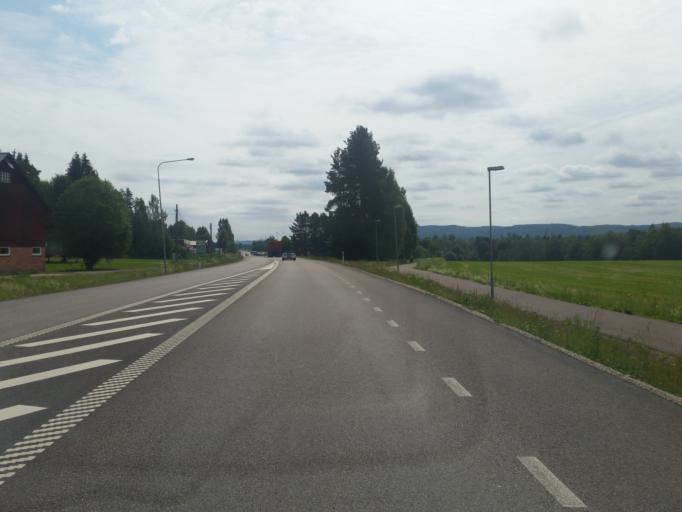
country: SE
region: Dalarna
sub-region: Gagnefs Kommun
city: Djuras
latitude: 60.5576
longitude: 15.1411
